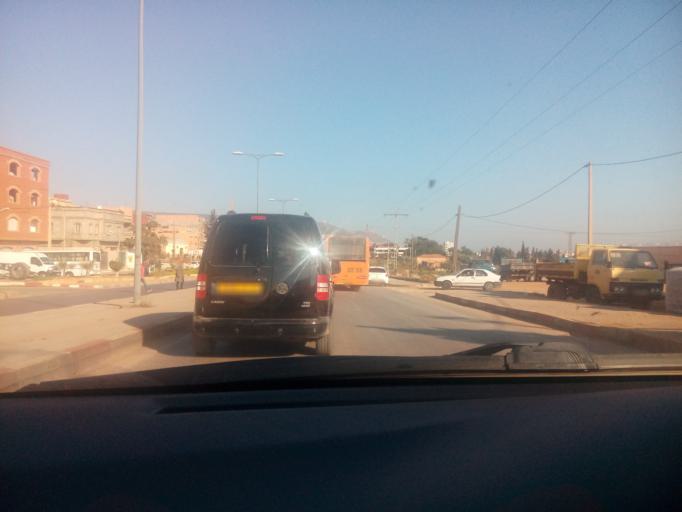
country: DZ
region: Oran
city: Oran
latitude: 35.6648
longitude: -0.6836
